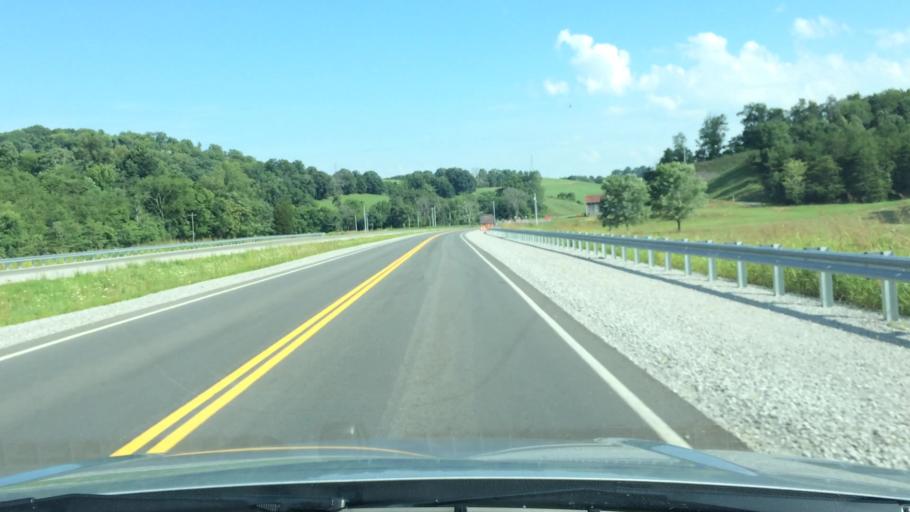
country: US
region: Tennessee
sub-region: Jefferson County
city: White Pine
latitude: 36.1382
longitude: -83.3415
